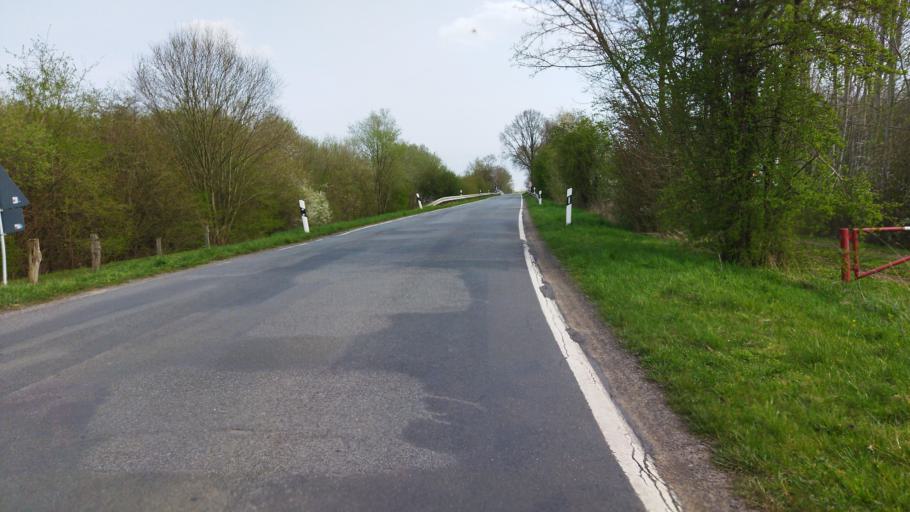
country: DE
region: Lower Saxony
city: Stolzenau
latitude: 52.4891
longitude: 9.0413
